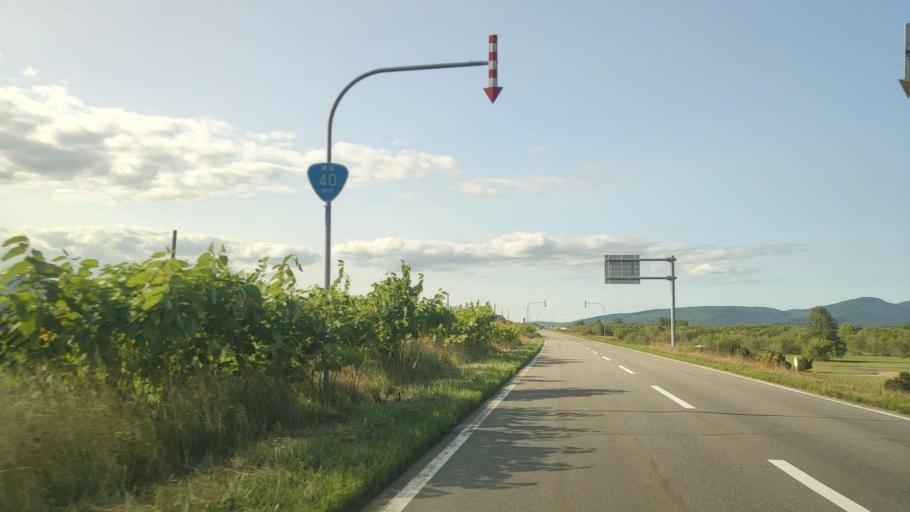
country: JP
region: Hokkaido
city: Nayoro
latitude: 44.8054
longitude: 142.0672
